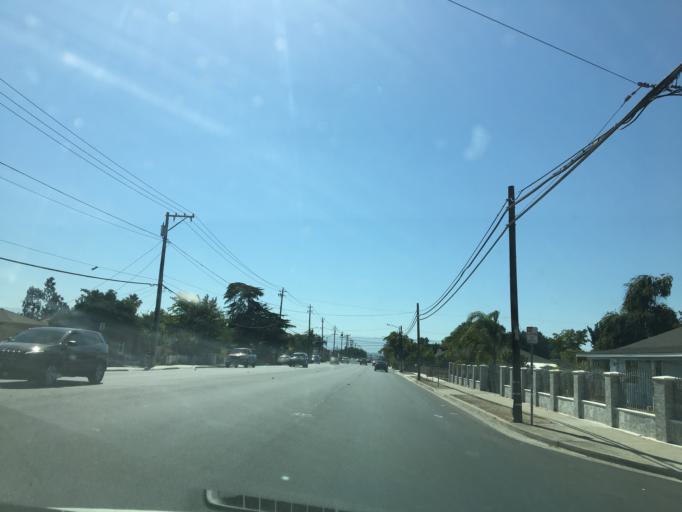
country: US
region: California
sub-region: Santa Clara County
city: Alum Rock
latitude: 37.3773
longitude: -121.8325
